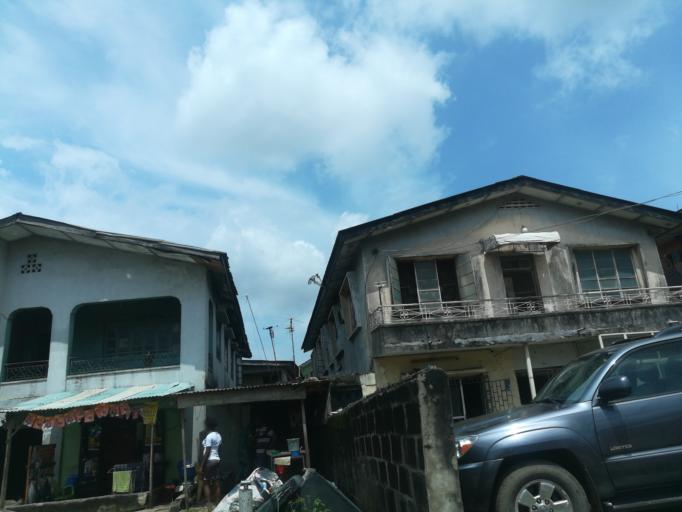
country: NG
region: Lagos
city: Somolu
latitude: 6.5368
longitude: 3.3649
